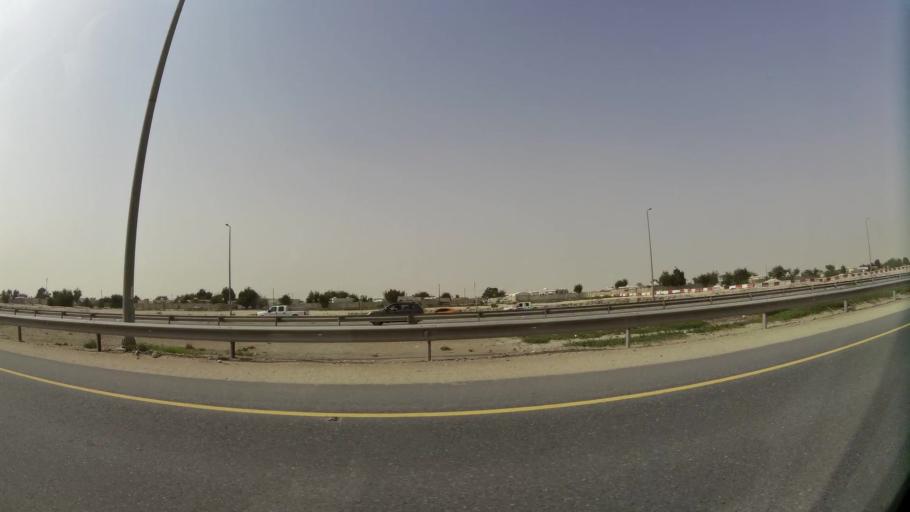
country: QA
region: Baladiyat ar Rayyan
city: Ar Rayyan
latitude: 25.1941
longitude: 51.3778
